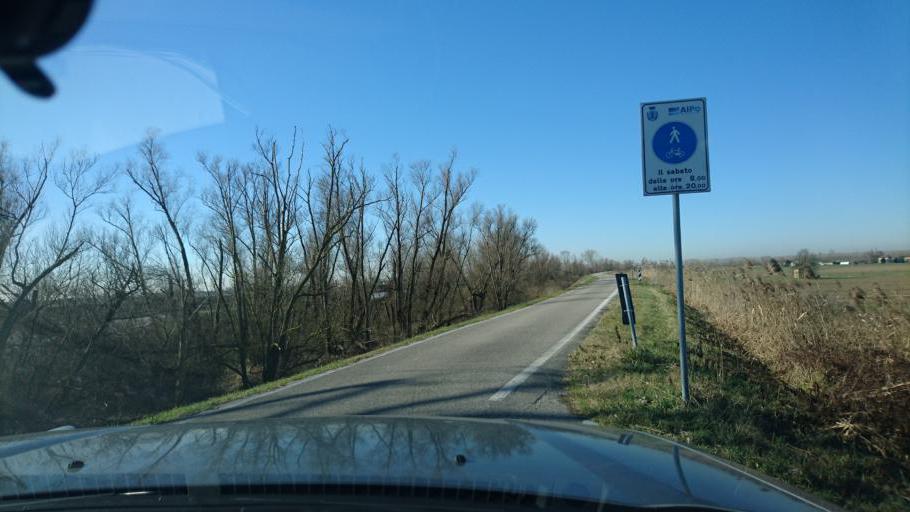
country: IT
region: Emilia-Romagna
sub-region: Provincia di Ferrara
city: Mesola
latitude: 44.9274
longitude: 12.2049
